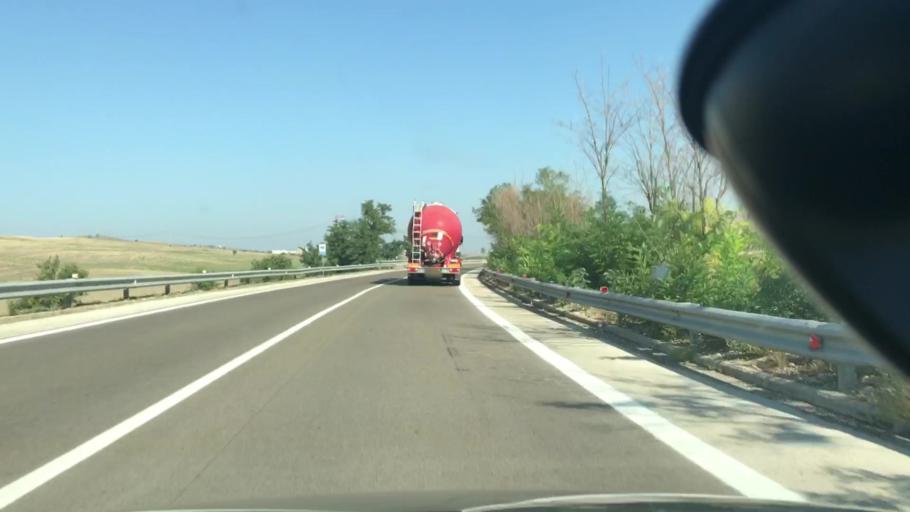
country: IT
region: Basilicate
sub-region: Provincia di Matera
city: Irsina
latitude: 40.7950
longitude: 16.2767
